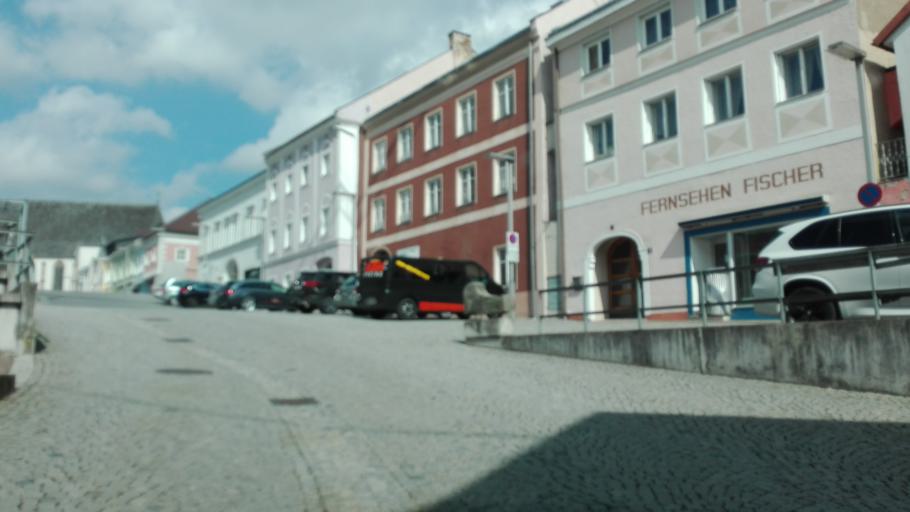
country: AT
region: Upper Austria
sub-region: Politischer Bezirk Urfahr-Umgebung
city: Ottensheim
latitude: 48.3309
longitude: 14.1766
